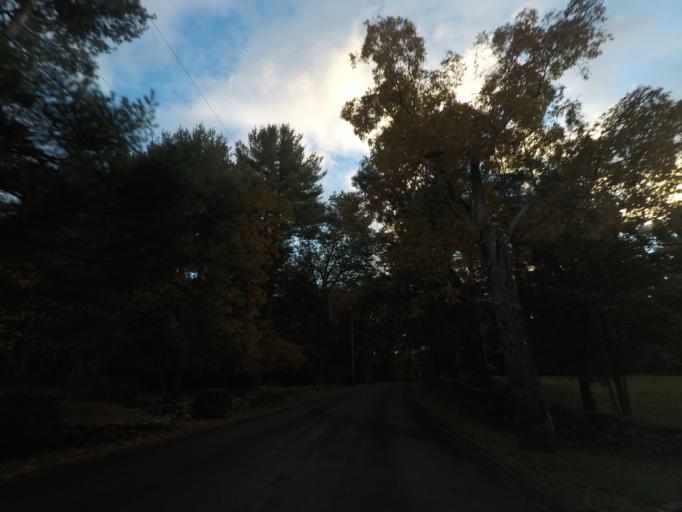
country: US
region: New York
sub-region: Rensselaer County
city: Nassau
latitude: 42.5326
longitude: -73.5788
